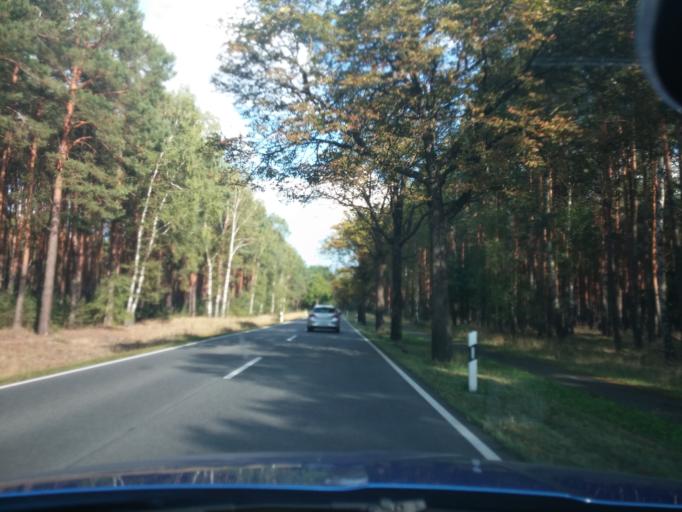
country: DE
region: Brandenburg
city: Halbe
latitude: 52.1067
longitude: 13.7171
